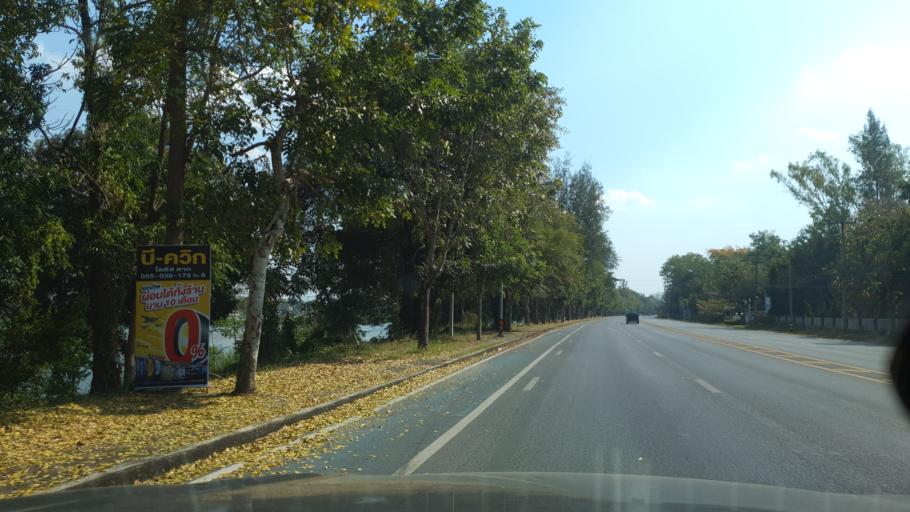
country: TH
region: Tak
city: Tak
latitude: 16.8756
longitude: 99.1169
